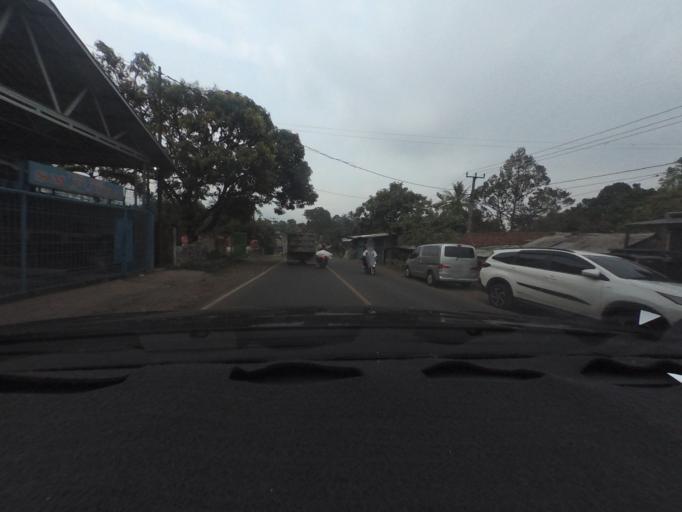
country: ID
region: West Java
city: Cicurug
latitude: -6.8126
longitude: 106.7695
